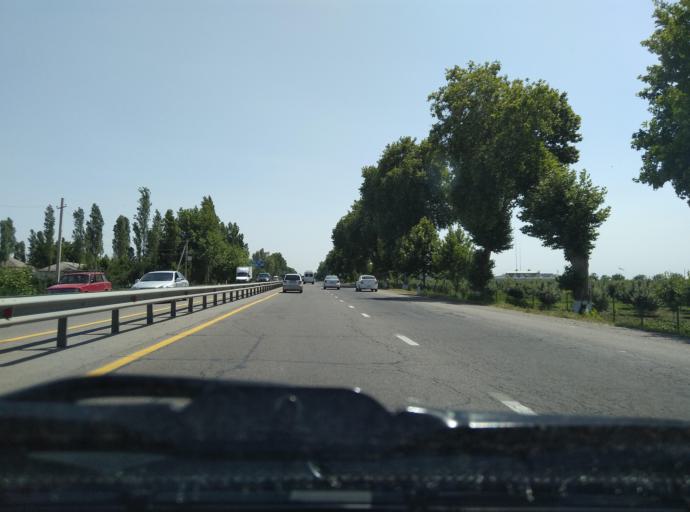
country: UZ
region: Toshkent Shahri
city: Bektemir
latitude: 41.2275
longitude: 69.4023
